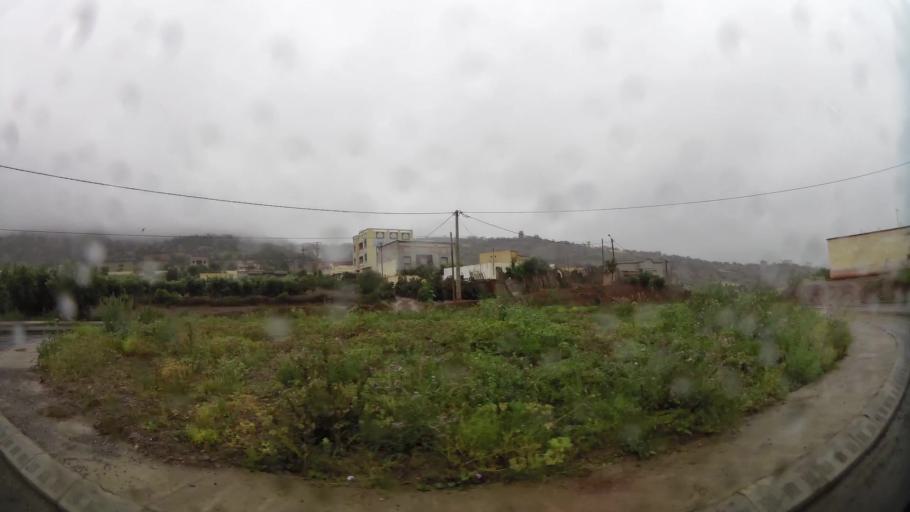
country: MA
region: Taza-Al Hoceima-Taounate
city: Imzourene
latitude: 35.0455
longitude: -3.8245
